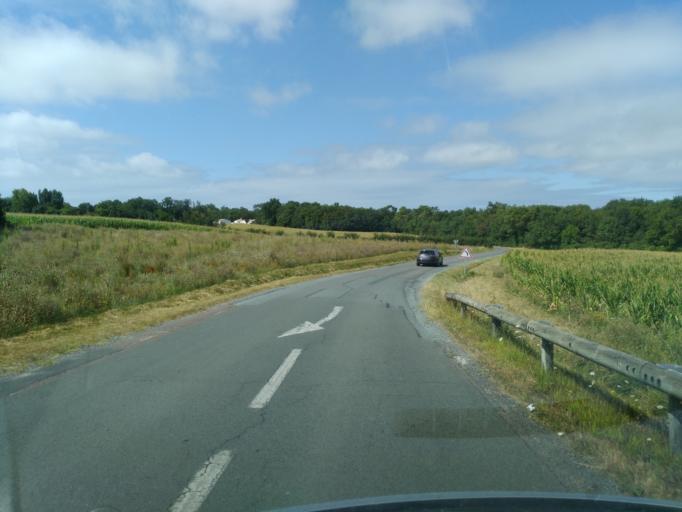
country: FR
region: Poitou-Charentes
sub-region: Departement de la Charente-Maritime
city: Breuillet
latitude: 45.7003
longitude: -1.0567
